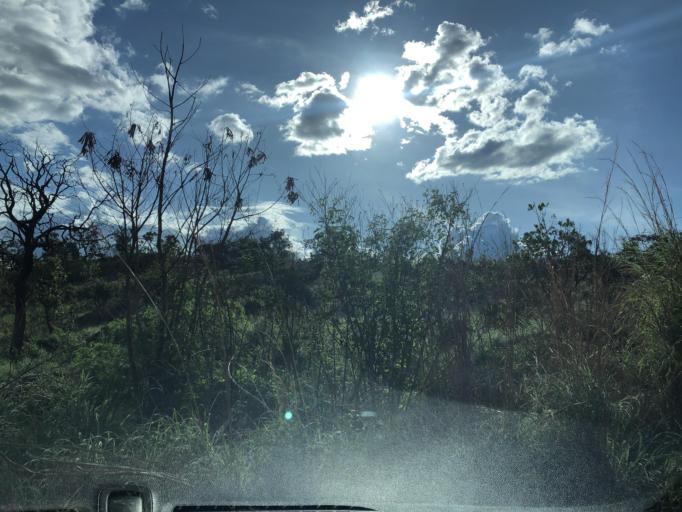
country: BR
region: Goias
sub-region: Luziania
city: Luziania
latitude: -16.0157
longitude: -48.1406
